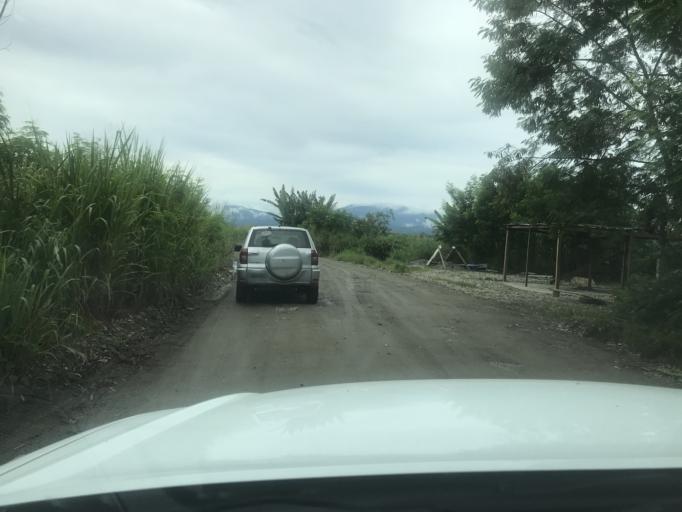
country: SB
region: Guadalcanal
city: Honiara
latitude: -9.4348
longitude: 160.0363
